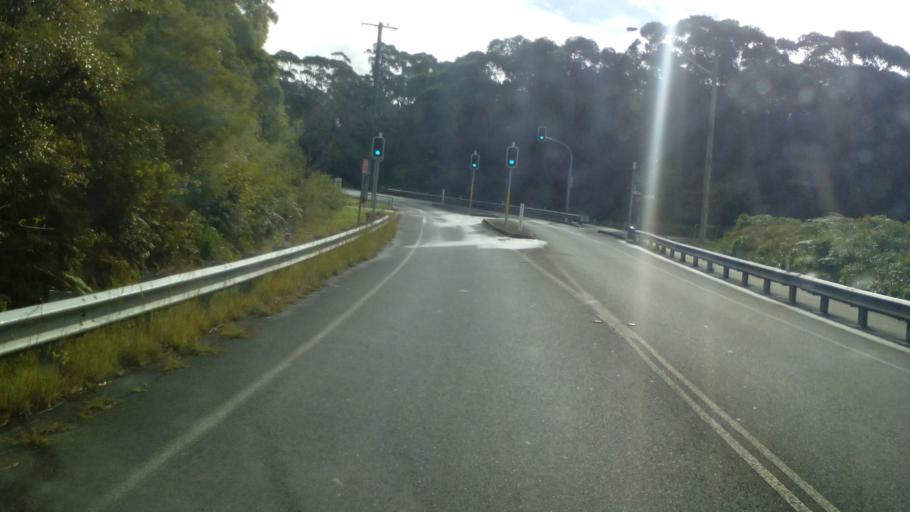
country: AU
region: New South Wales
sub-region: Lake Macquarie Shire
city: Kahibah
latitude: -32.9622
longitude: 151.7190
